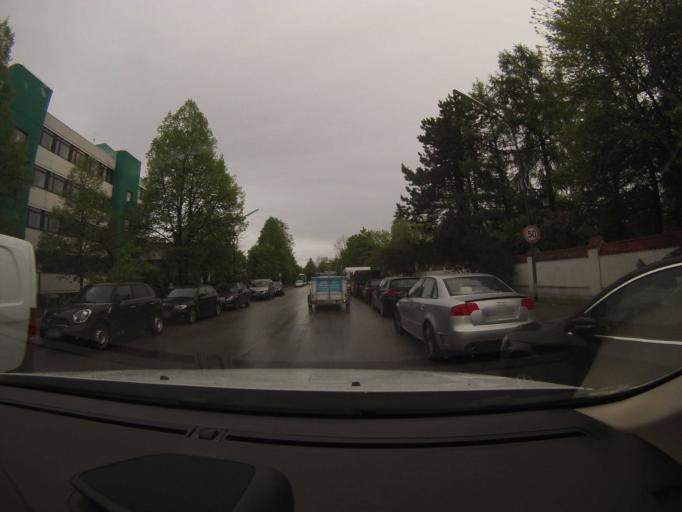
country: DE
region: Bavaria
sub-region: Upper Bavaria
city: Taufkirchen
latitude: 48.0578
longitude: 11.6258
